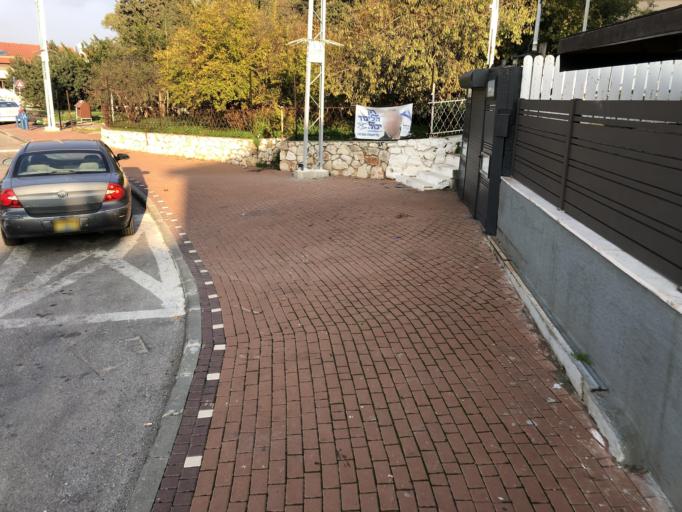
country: IL
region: Northern District
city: `Akko
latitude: 32.9244
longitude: 35.0872
